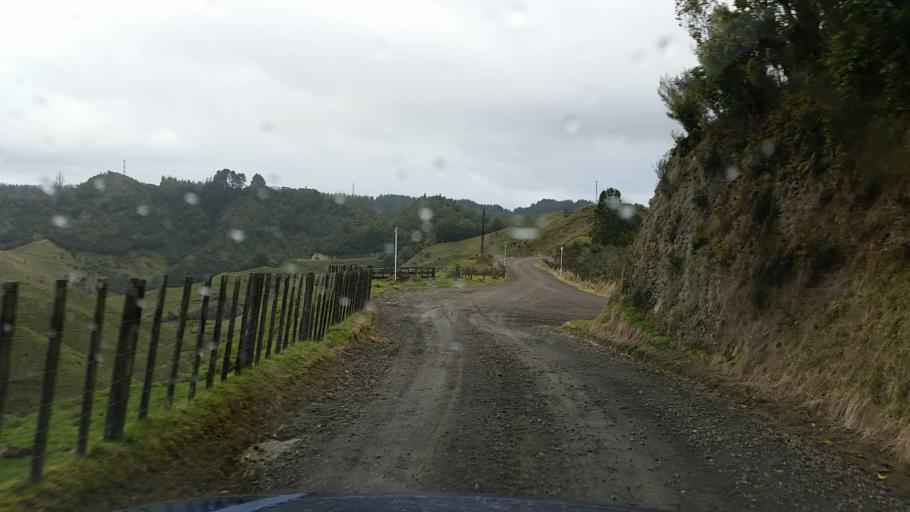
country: NZ
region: Taranaki
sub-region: South Taranaki District
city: Eltham
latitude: -39.1713
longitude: 174.6262
